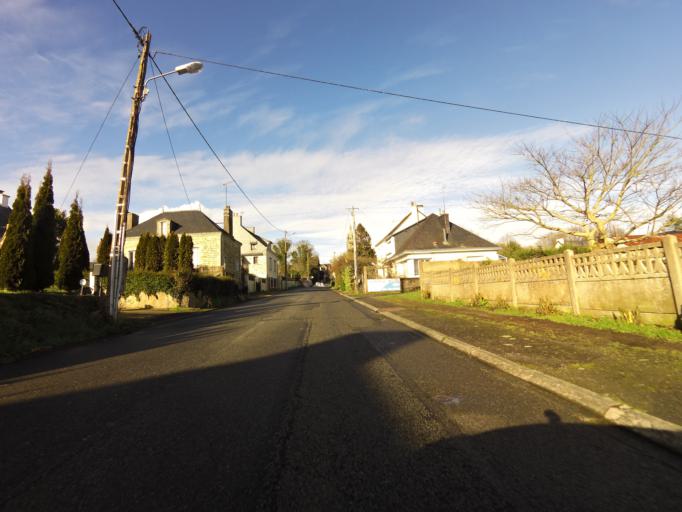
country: FR
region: Brittany
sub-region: Departement du Morbihan
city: Limerzel
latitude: 47.6336
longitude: -2.3544
